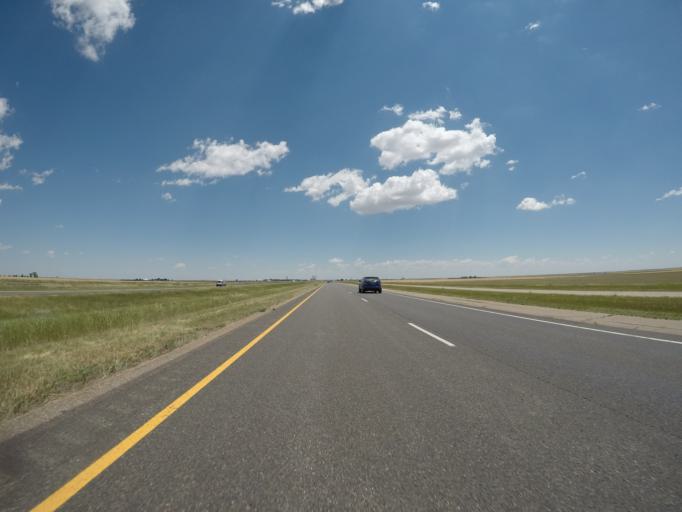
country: US
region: Colorado
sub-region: Lincoln County
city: Hugo
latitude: 39.2820
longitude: -103.3081
